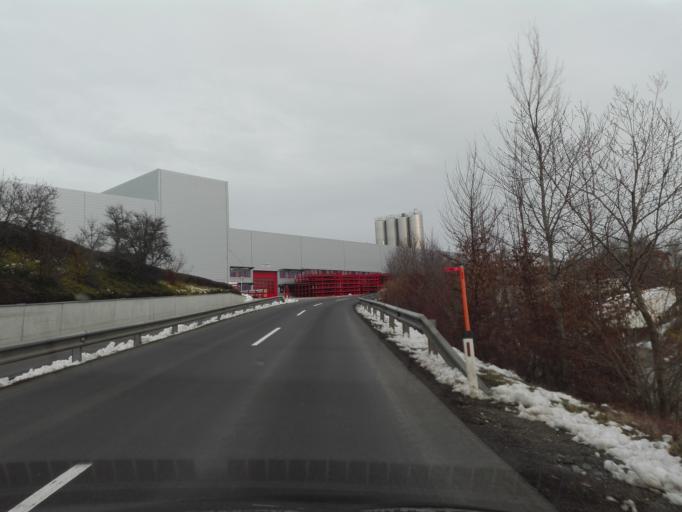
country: AT
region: Upper Austria
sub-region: Politischer Bezirk Rohrbach
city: Atzesberg
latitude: 48.5478
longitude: 13.8940
